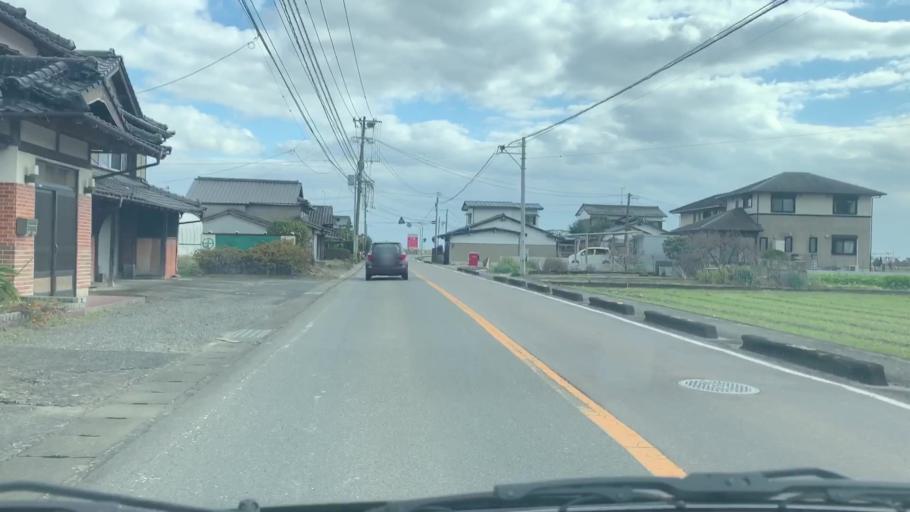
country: JP
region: Saga Prefecture
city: Takeocho-takeo
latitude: 33.2054
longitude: 130.0898
